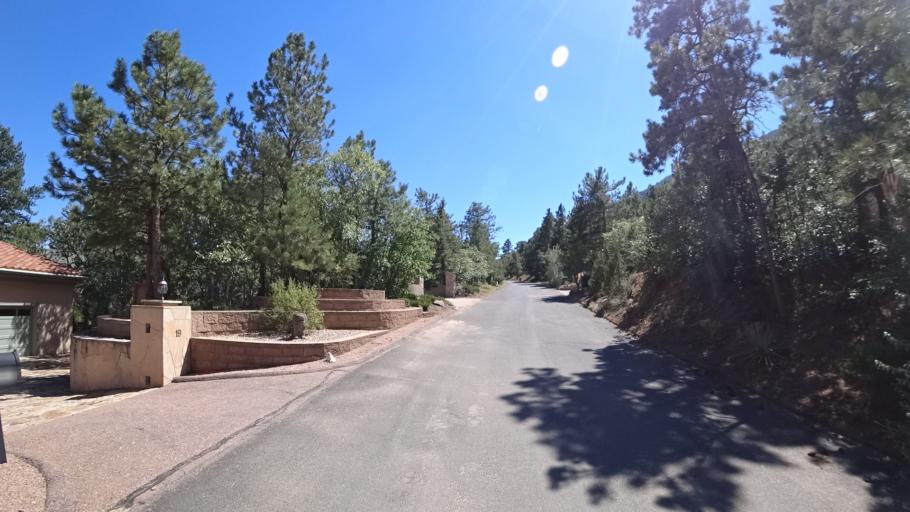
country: US
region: Colorado
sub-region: El Paso County
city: Colorado Springs
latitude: 38.7823
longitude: -104.8606
